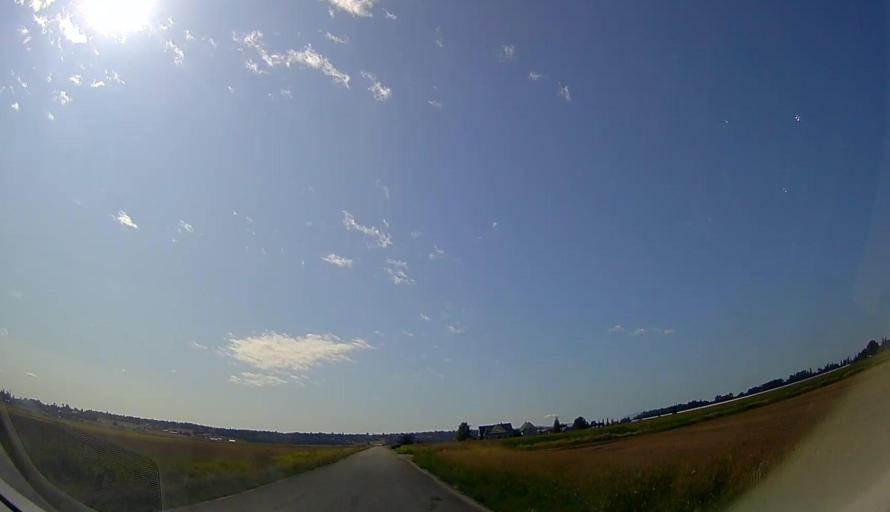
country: US
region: Washington
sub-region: Skagit County
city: Burlington
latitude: 48.4939
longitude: -122.3719
